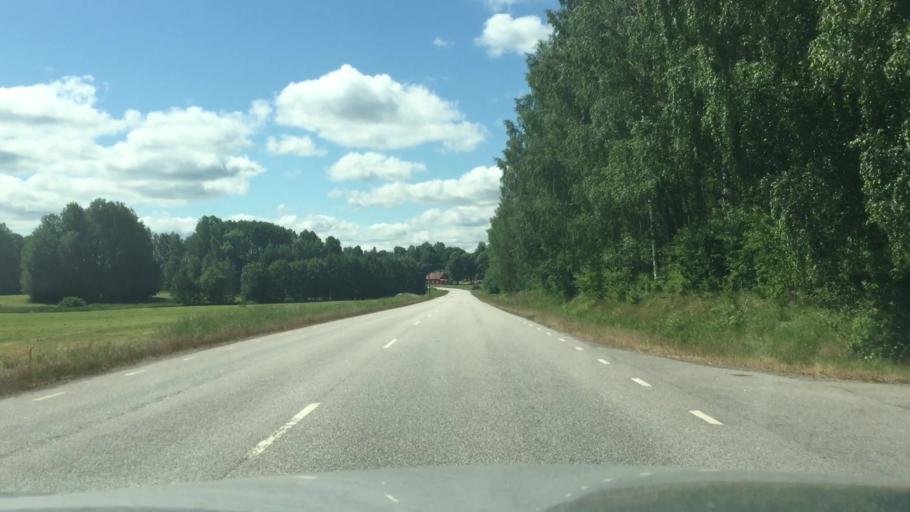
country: SE
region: Vaestra Goetaland
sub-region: Karlsborgs Kommun
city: Molltorp
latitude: 58.6342
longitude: 14.3920
